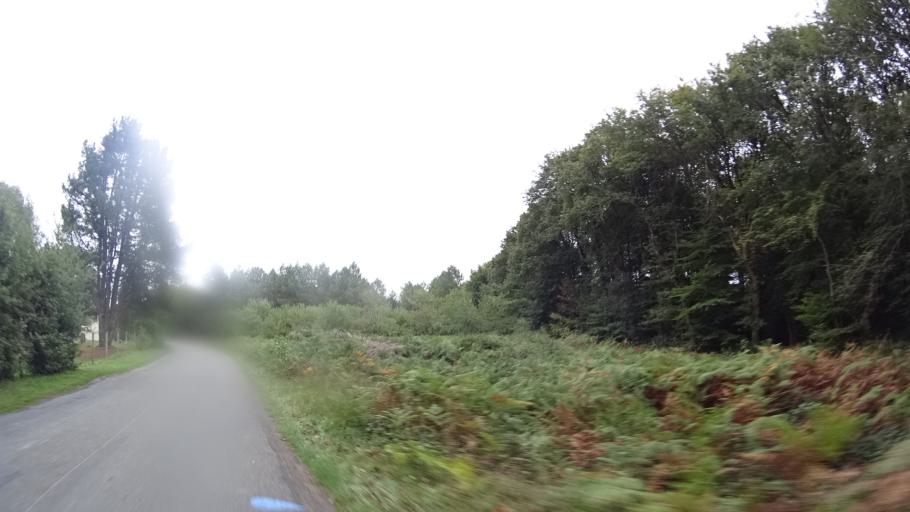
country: FR
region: Brittany
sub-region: Departement d'Ille-et-Vilaine
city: Paimpont
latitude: 48.0834
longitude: -2.1376
